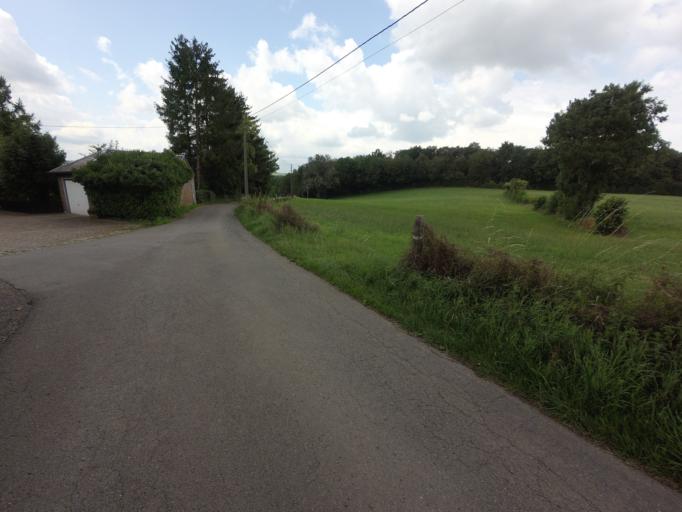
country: BE
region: Wallonia
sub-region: Province de Liege
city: La Calamine
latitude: 50.7059
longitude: 5.9800
